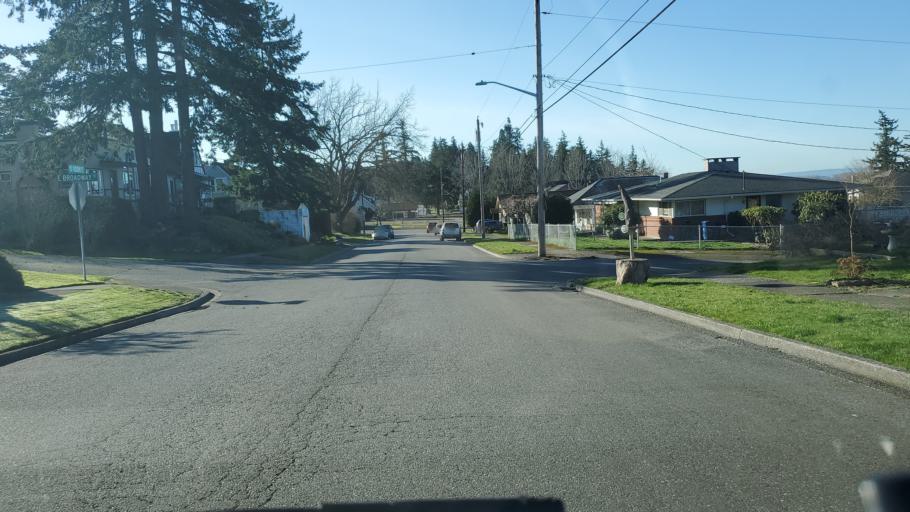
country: US
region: Washington
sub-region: Skagit County
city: Mount Vernon
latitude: 48.4168
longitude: -122.3287
